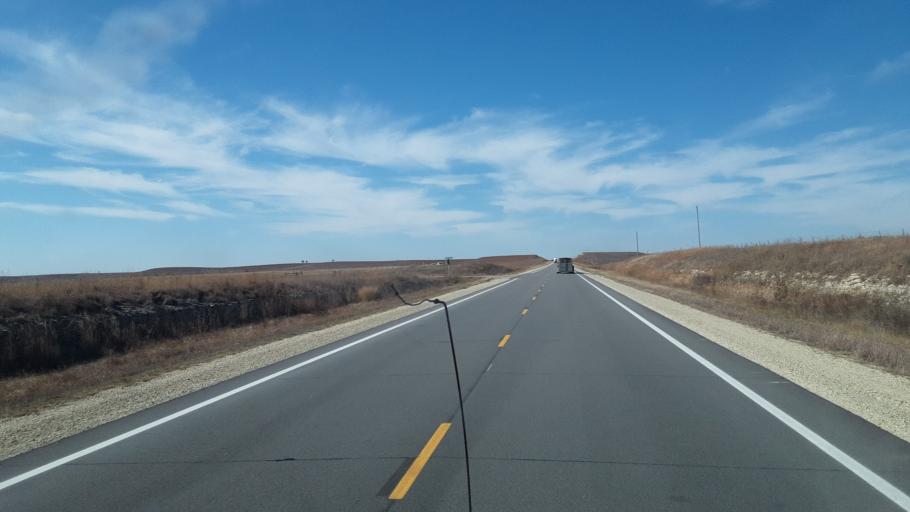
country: US
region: Kansas
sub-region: Chase County
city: Cottonwood Falls
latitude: 38.3627
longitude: -96.7538
